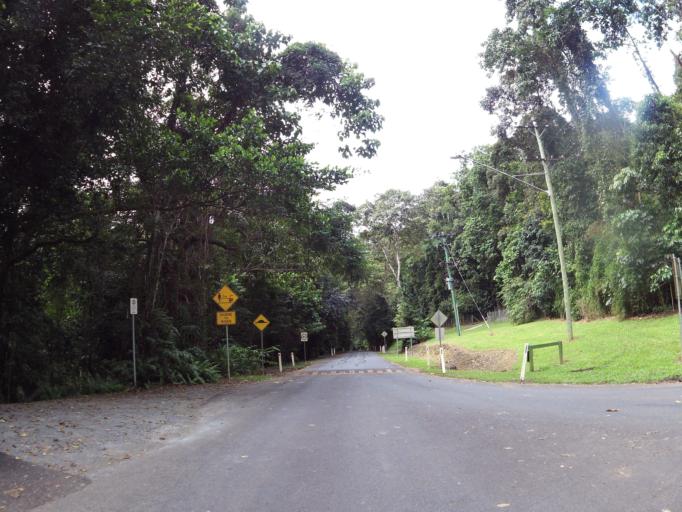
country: AU
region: Queensland
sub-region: Cairns
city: Woree
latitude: -16.9618
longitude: 145.6800
